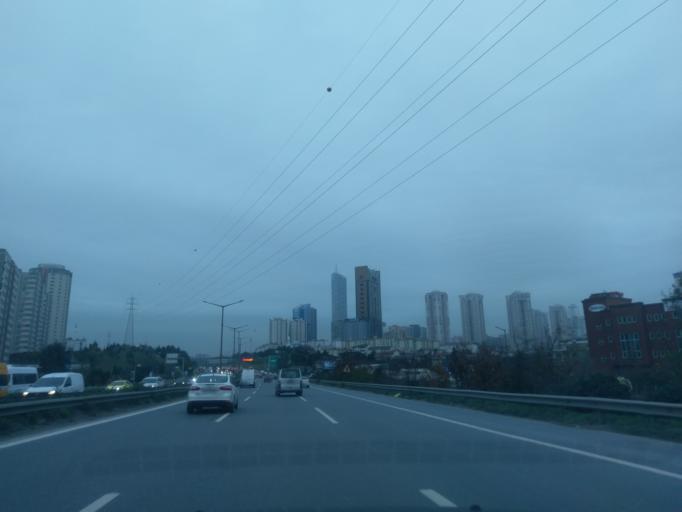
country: TR
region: Istanbul
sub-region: Atasehir
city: Atasehir
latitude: 40.9860
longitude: 29.1061
